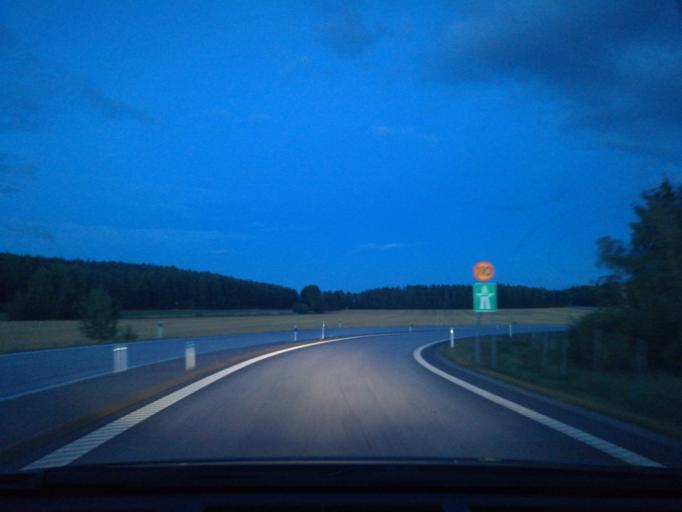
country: SE
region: Uppsala
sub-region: Habo Kommun
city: Balsta
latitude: 59.5875
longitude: 17.5094
